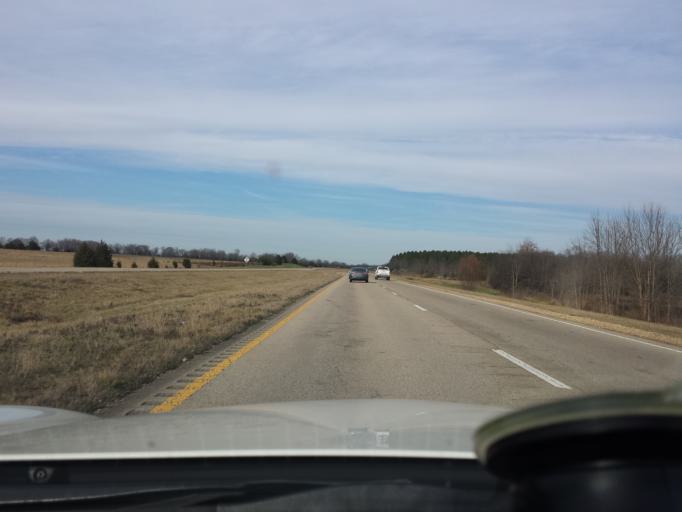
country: US
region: Mississippi
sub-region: Lee County
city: Shannon
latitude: 34.0615
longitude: -88.7030
